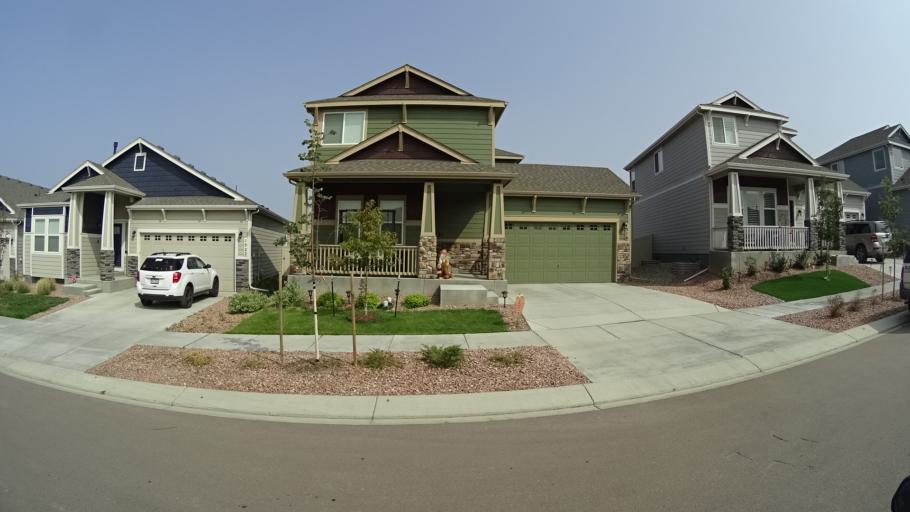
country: US
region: Colorado
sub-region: El Paso County
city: Stratmoor
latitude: 38.8098
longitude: -104.7909
